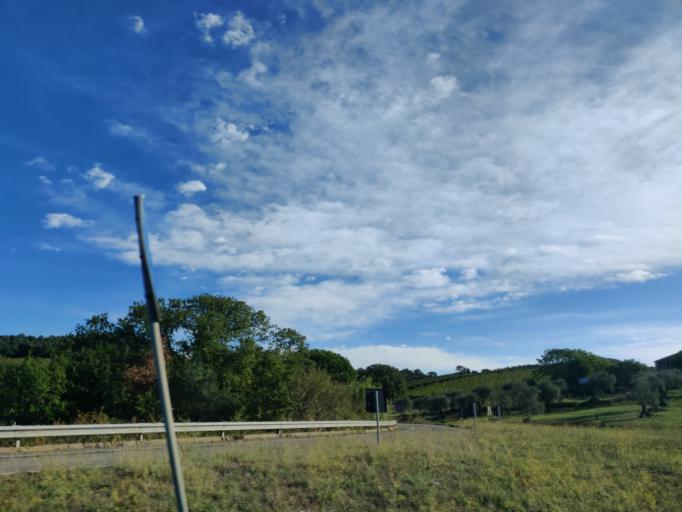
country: IT
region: Tuscany
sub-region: Provincia di Grosseto
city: Gavorrano
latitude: 42.9501
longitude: 10.9299
